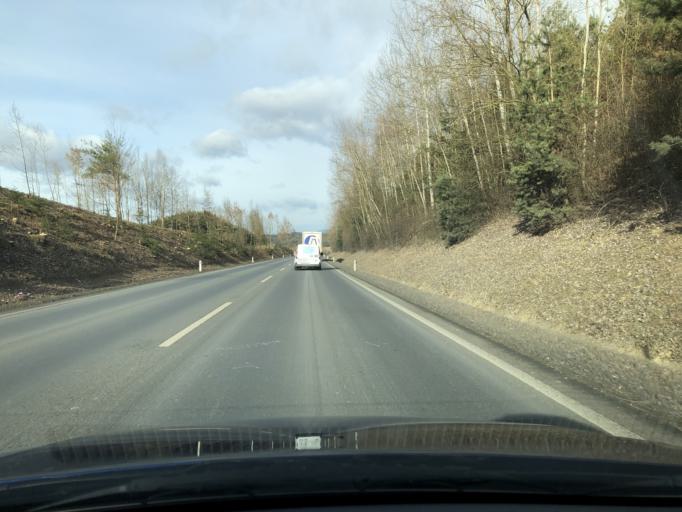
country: AT
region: Burgenland
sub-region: Politischer Bezirk Oberwart
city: Oberwart
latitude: 47.2776
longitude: 16.1950
